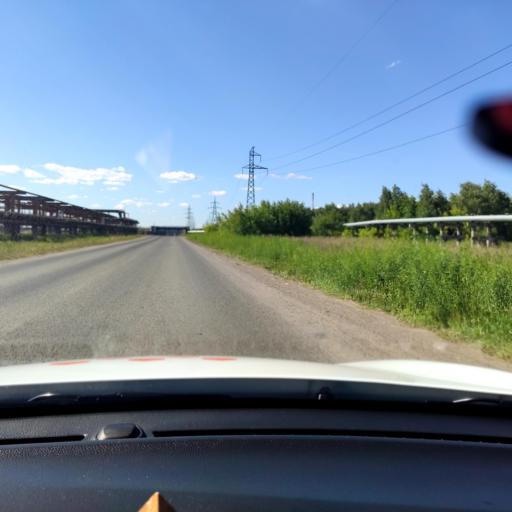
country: RU
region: Tatarstan
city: Staroye Arakchino
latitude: 55.8747
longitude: 48.9750
